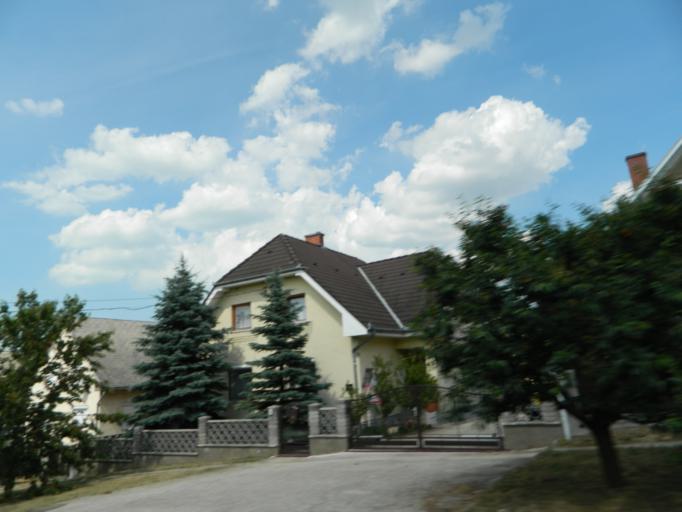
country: HU
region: Somogy
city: Balatonfoldvar
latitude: 46.8229
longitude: 17.9050
